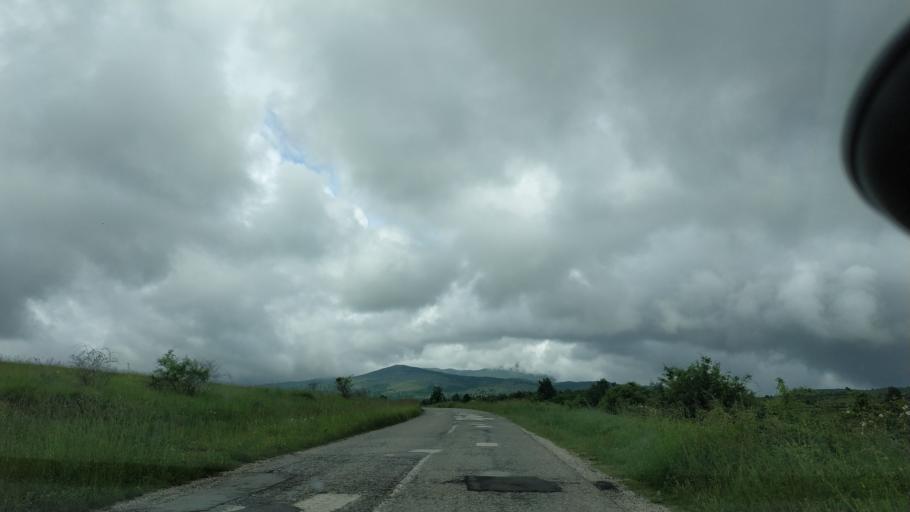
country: RS
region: Central Serbia
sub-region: Zajecarski Okrug
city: Soko Banja
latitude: 43.6997
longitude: 21.9376
